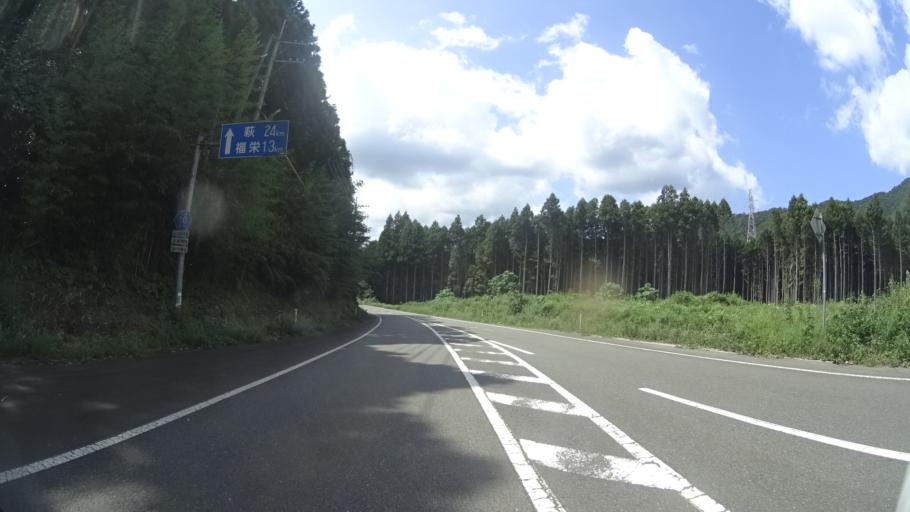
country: JP
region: Yamaguchi
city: Hagi
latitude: 34.4985
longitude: 131.5548
